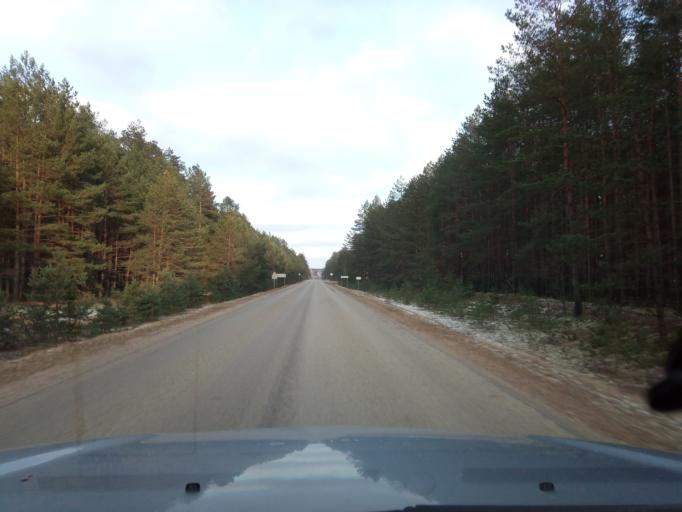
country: LT
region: Alytaus apskritis
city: Varena
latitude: 54.2096
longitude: 24.5474
